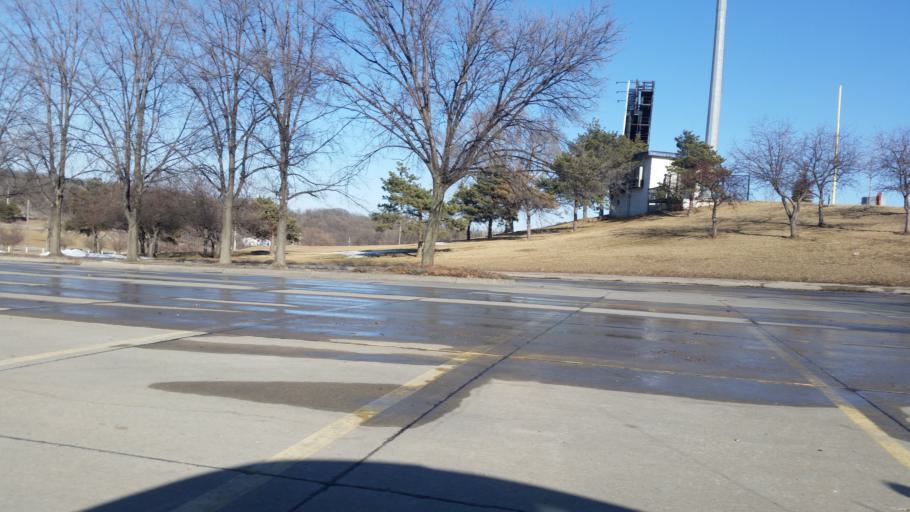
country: US
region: Nebraska
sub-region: Douglas County
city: Omaha
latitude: 41.2266
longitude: -95.9328
